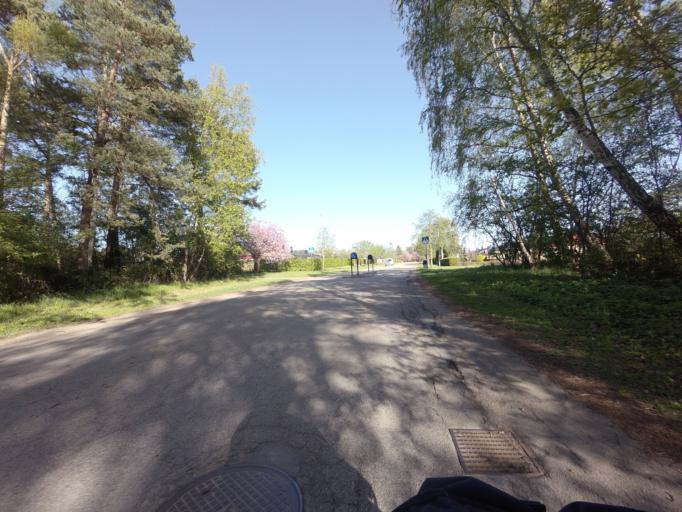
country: SE
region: Skane
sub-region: Landskrona
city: Asmundtorp
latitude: 55.8496
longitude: 12.9150
